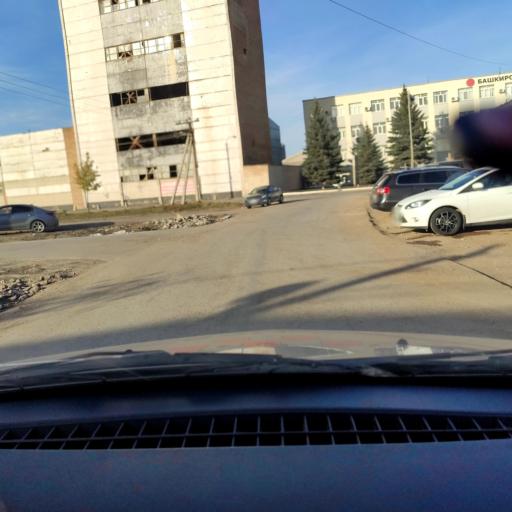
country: RU
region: Bashkortostan
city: Ufa
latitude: 54.7453
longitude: 55.9184
